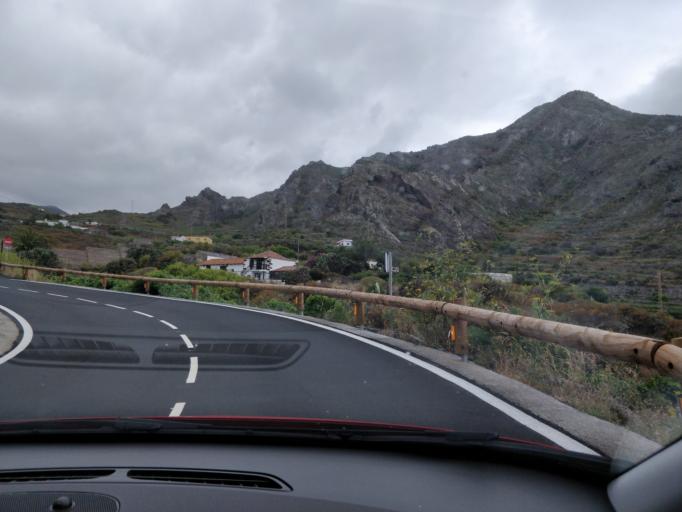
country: ES
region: Canary Islands
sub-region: Provincia de Santa Cruz de Tenerife
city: Tanque
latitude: 28.3548
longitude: -16.8456
